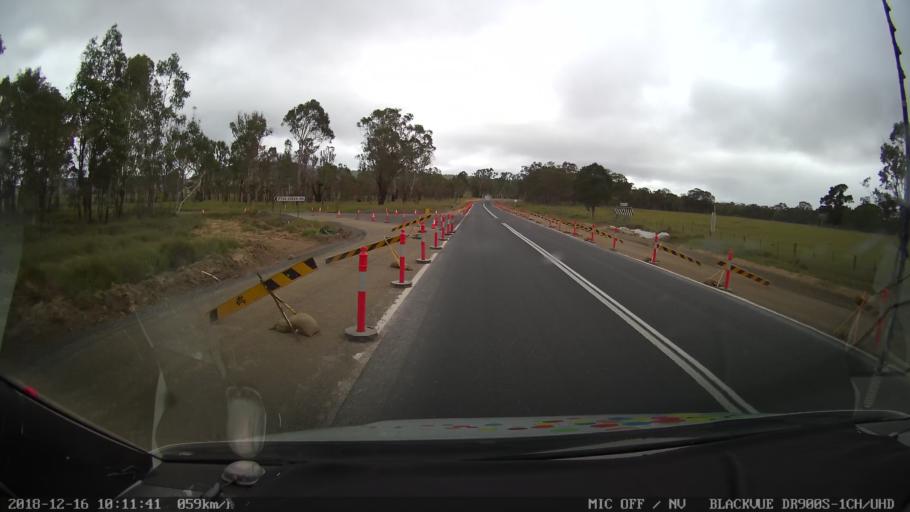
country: AU
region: New South Wales
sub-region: Glen Innes Severn
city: Glen Innes
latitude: -29.3115
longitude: 151.9343
